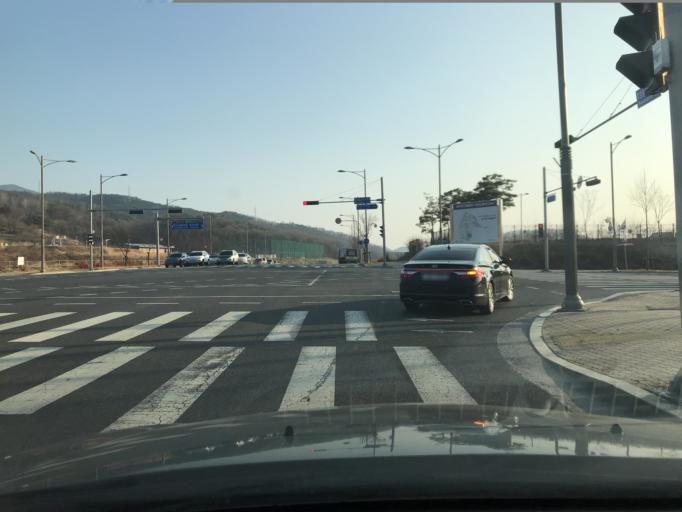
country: KR
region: Daegu
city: Hwawon
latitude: 35.6896
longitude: 128.4699
